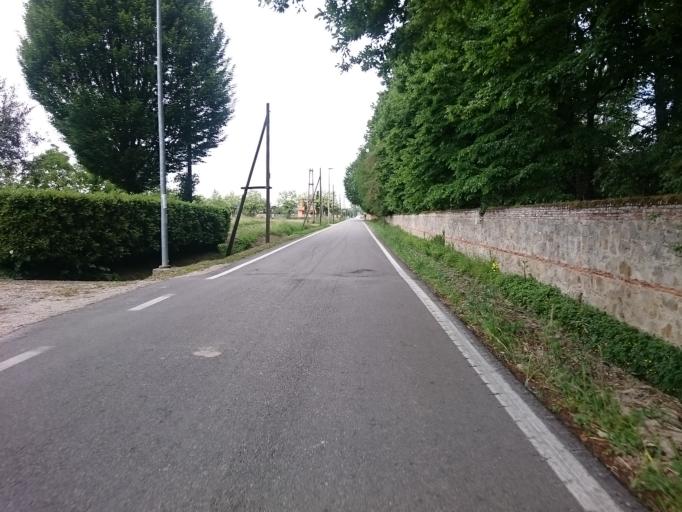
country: IT
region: Veneto
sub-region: Provincia di Padova
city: Granze
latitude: 45.1518
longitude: 11.7188
